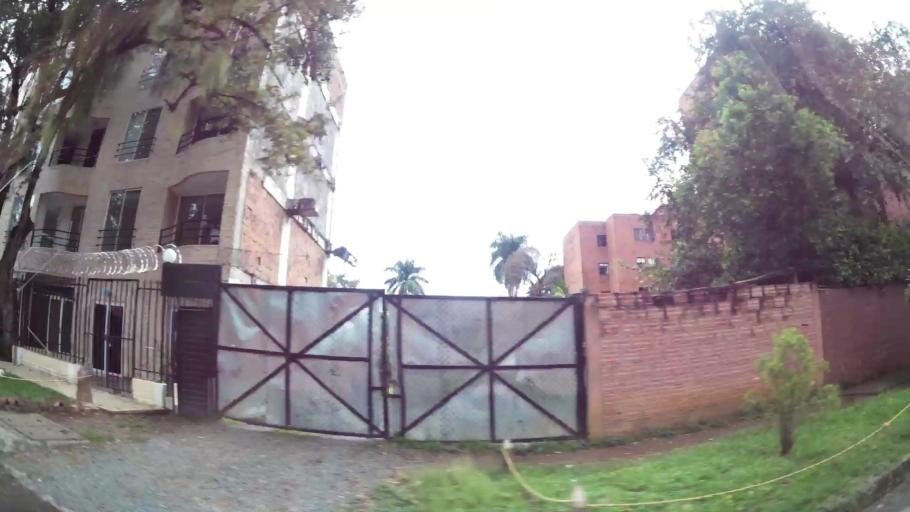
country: CO
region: Valle del Cauca
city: Cali
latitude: 3.3965
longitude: -76.5541
